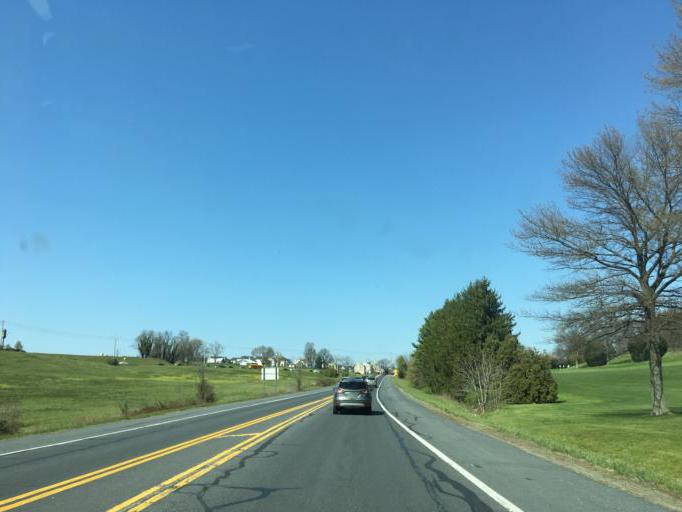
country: US
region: Maryland
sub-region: Carroll County
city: Westminster
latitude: 39.5856
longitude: -77.0082
